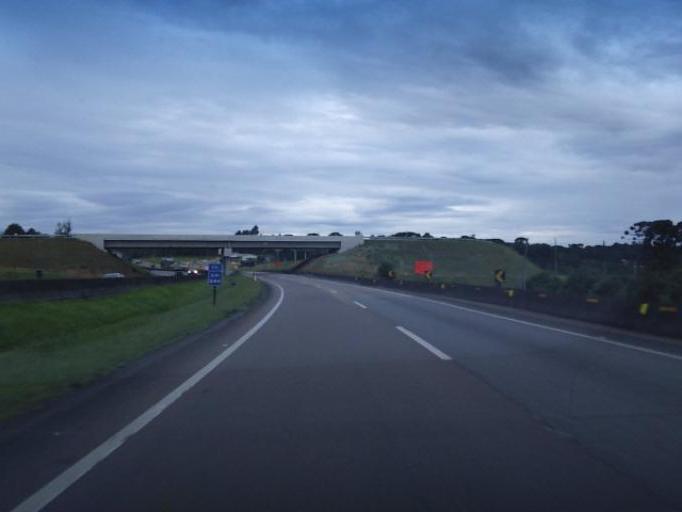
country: BR
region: Parana
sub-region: Sao Jose Dos Pinhais
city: Sao Jose dos Pinhais
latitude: -25.8206
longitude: -49.1283
